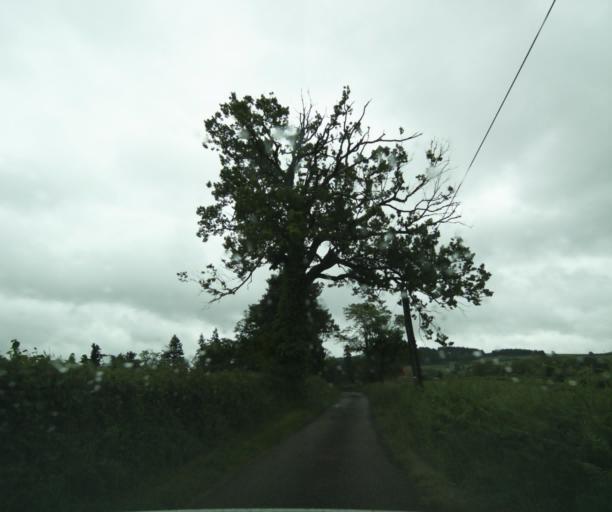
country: FR
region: Bourgogne
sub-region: Departement de Saone-et-Loire
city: Matour
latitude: 46.4635
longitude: 4.4765
